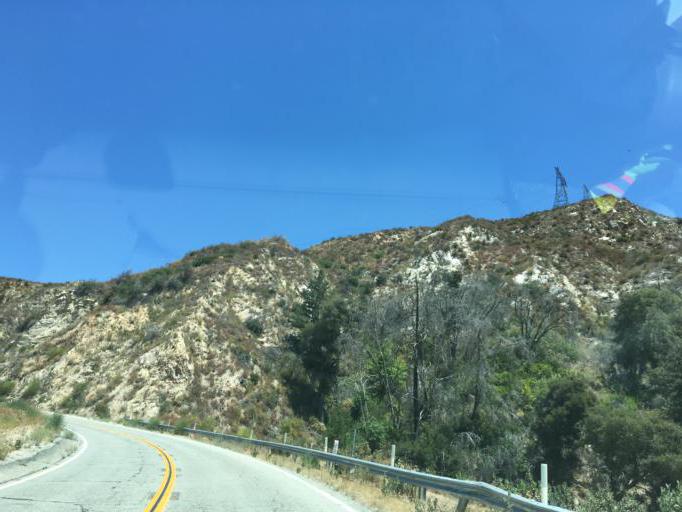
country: US
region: California
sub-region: Los Angeles County
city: La Crescenta-Montrose
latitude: 34.2917
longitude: -118.1819
